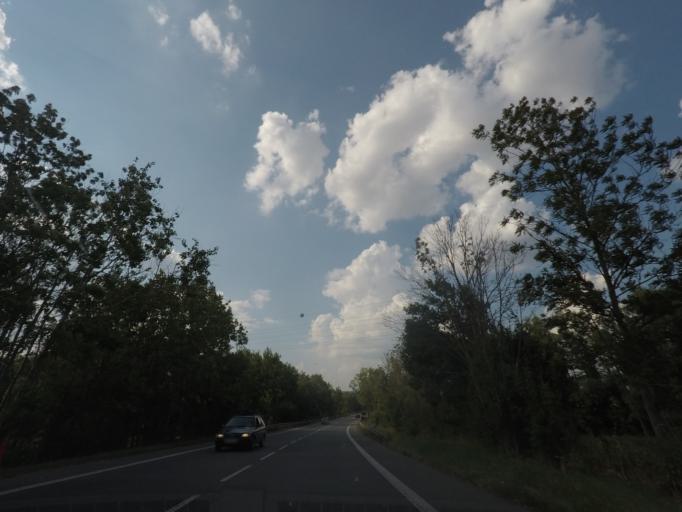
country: CZ
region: Kralovehradecky
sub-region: Okres Nachod
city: Jaromer
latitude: 50.4068
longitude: 15.8867
